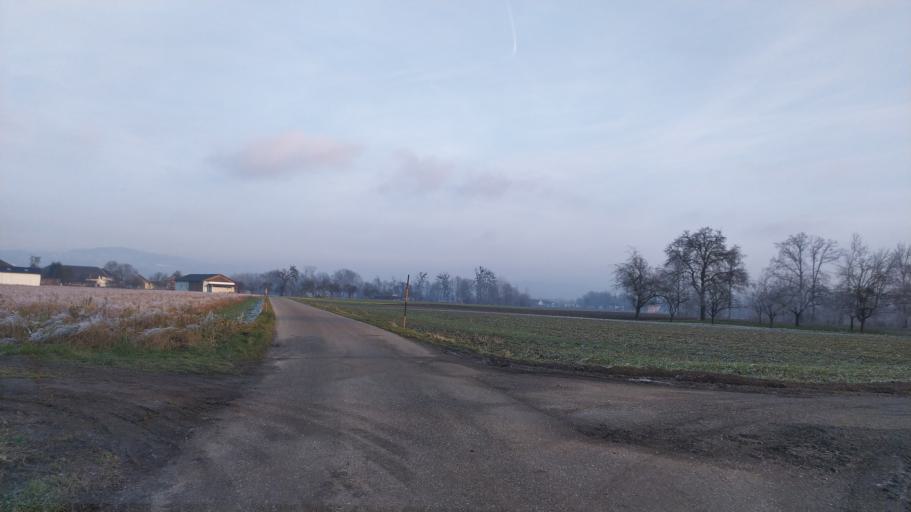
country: AT
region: Upper Austria
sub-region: Politischer Bezirk Urfahr-Umgebung
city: Goldworth
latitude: 48.3280
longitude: 14.1225
